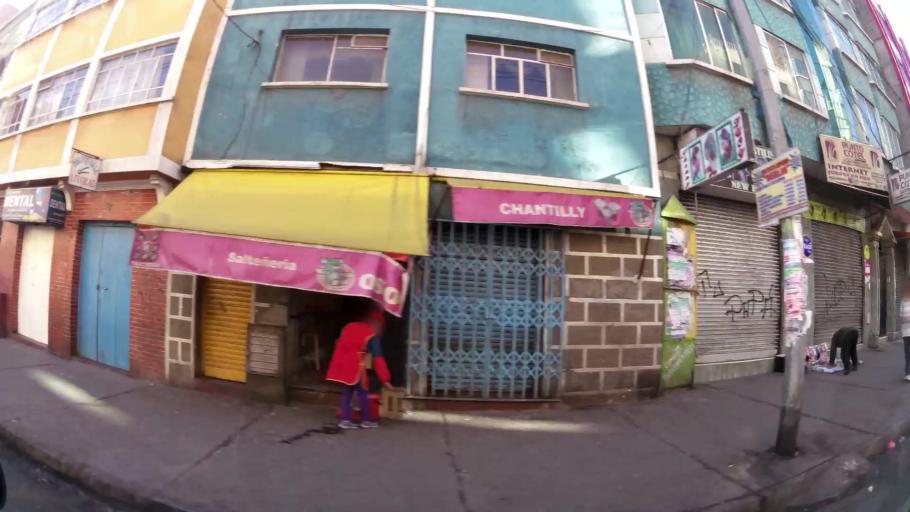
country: BO
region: La Paz
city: La Paz
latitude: -16.5006
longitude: -68.1453
